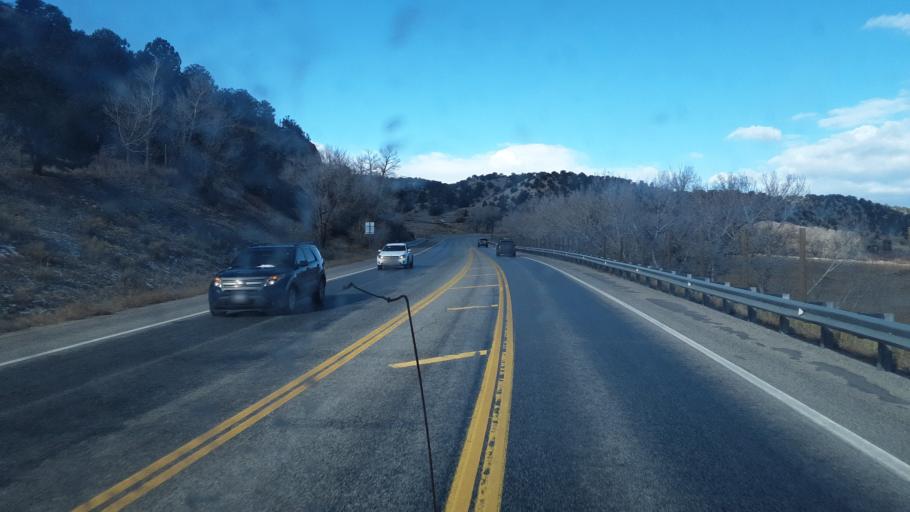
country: US
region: Colorado
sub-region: Chaffee County
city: Buena Vista
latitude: 38.7797
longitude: -106.1090
